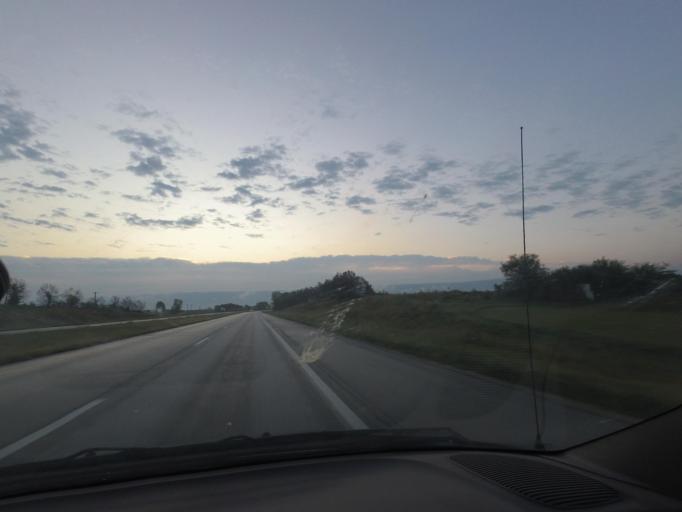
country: US
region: Missouri
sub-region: Macon County
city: Macon
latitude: 39.7600
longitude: -92.5567
